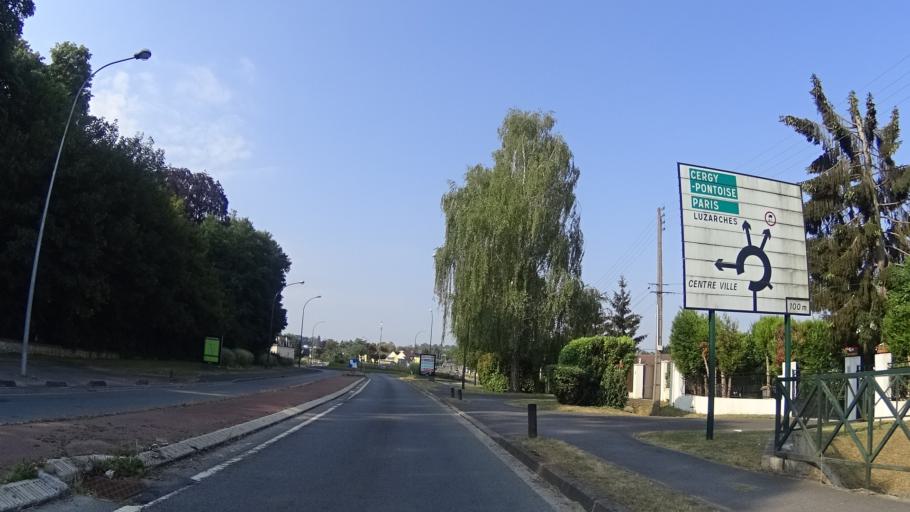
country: FR
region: Ile-de-France
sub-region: Departement du Val-d'Oise
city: Chaumontel
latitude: 49.1245
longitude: 2.4278
